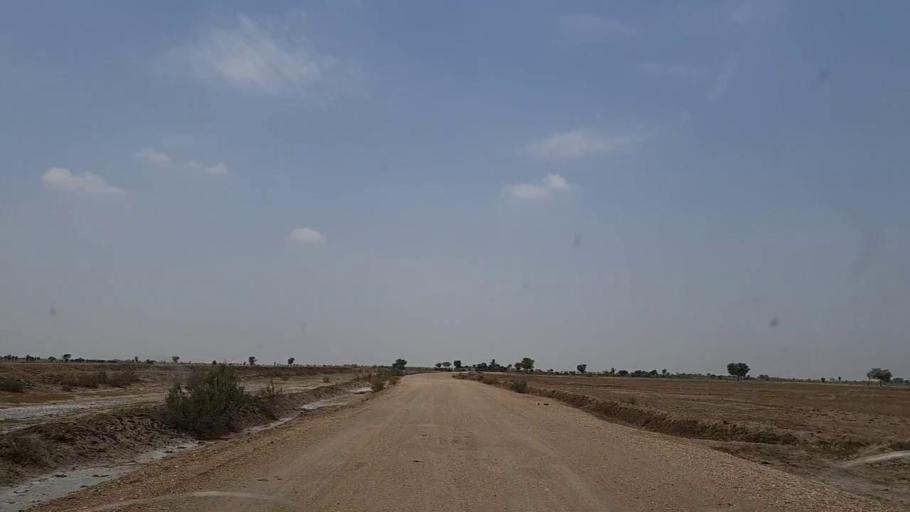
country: PK
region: Sindh
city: Phulji
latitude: 26.8009
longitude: 67.6357
